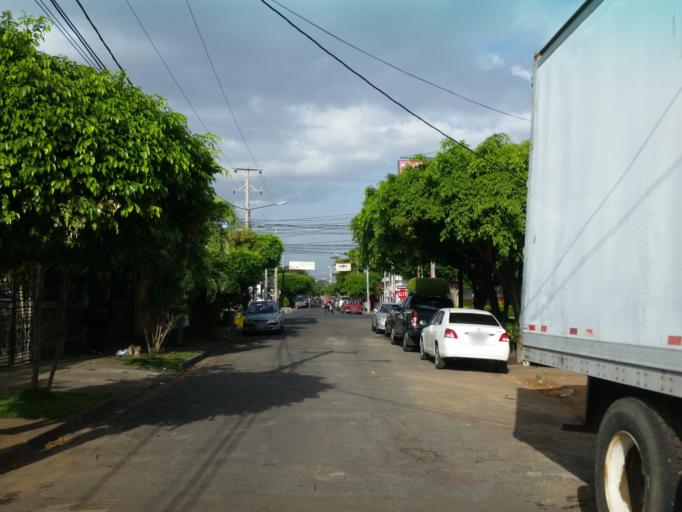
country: NI
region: Managua
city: Managua
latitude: 12.1215
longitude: -86.2531
